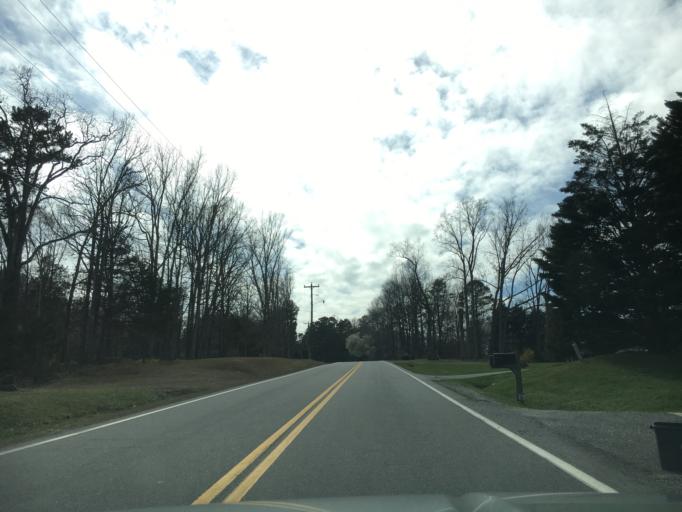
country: US
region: Virginia
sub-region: Halifax County
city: Halifax
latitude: 36.7579
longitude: -78.9126
